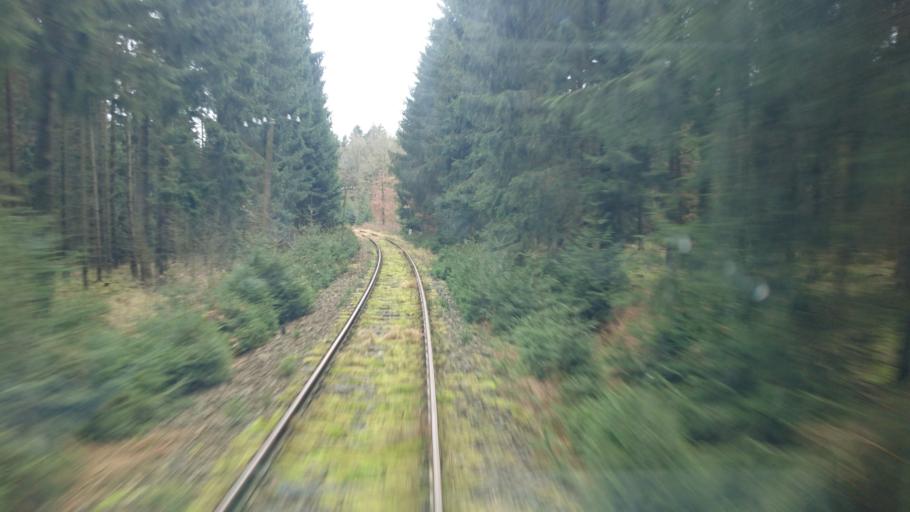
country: DE
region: Saxony
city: Muhltroff
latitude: 50.5533
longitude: 11.9064
